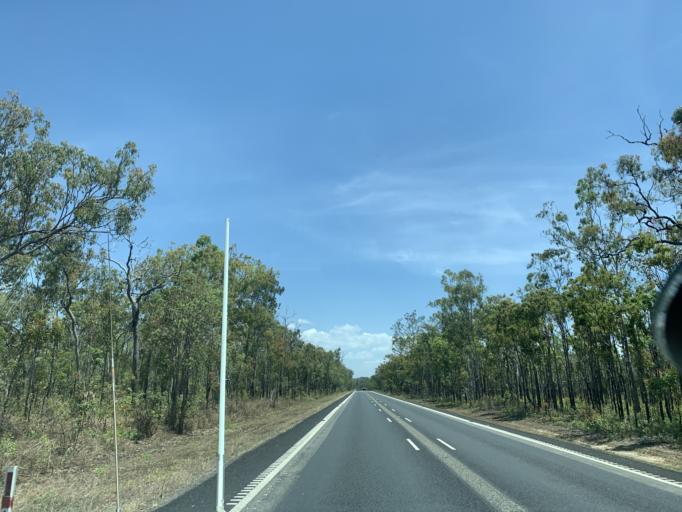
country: AU
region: Queensland
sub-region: Tablelands
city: Kuranda
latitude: -16.9273
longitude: 145.5487
